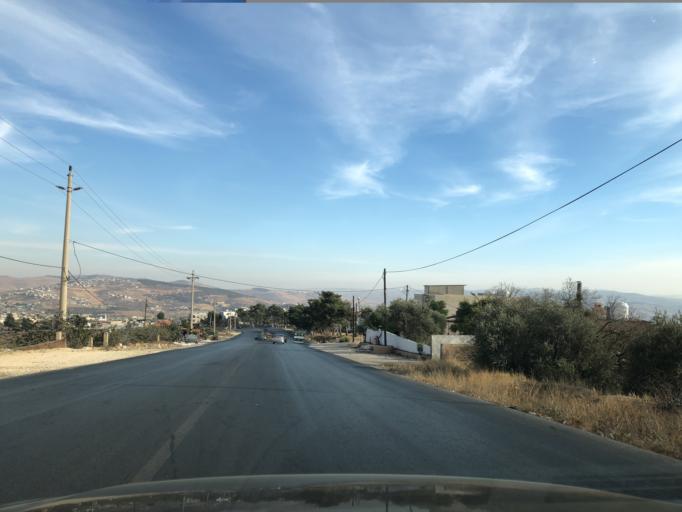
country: JO
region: Irbid
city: Al Kittah
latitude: 32.2800
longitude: 35.8671
